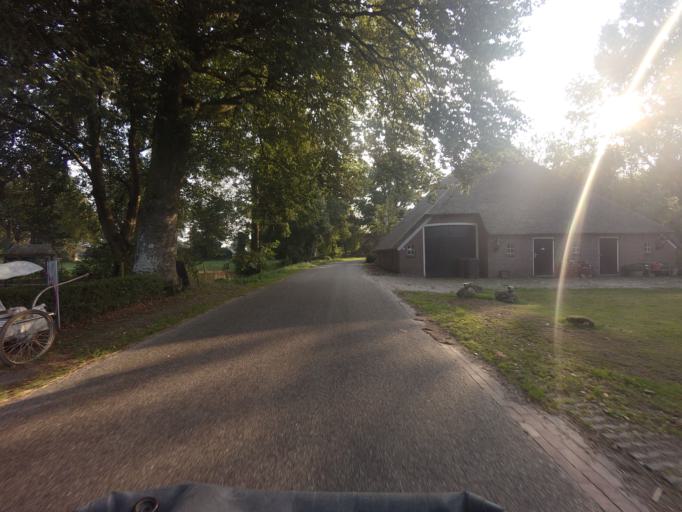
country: NL
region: Drenthe
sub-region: Gemeente Tynaarlo
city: Vries
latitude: 53.1140
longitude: 6.5248
